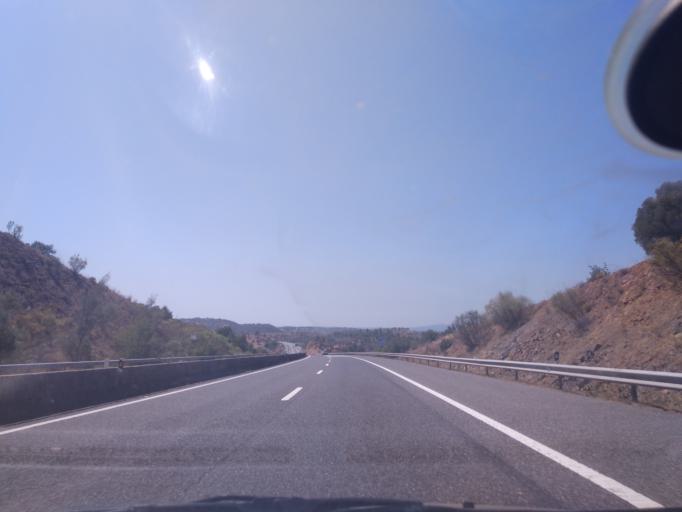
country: PT
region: Faro
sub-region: Portimao
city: Portimao
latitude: 37.1719
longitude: -8.5168
